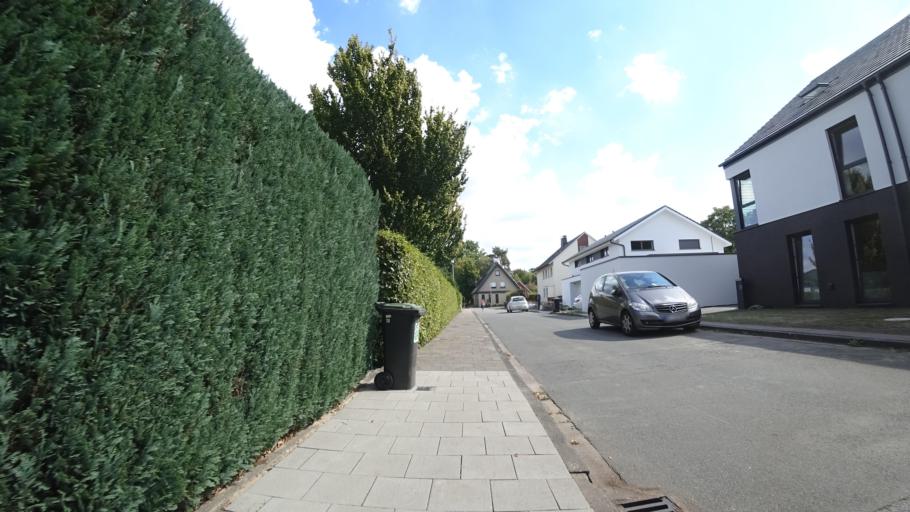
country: DE
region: North Rhine-Westphalia
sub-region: Regierungsbezirk Detmold
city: Verl
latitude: 51.9409
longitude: 8.4796
